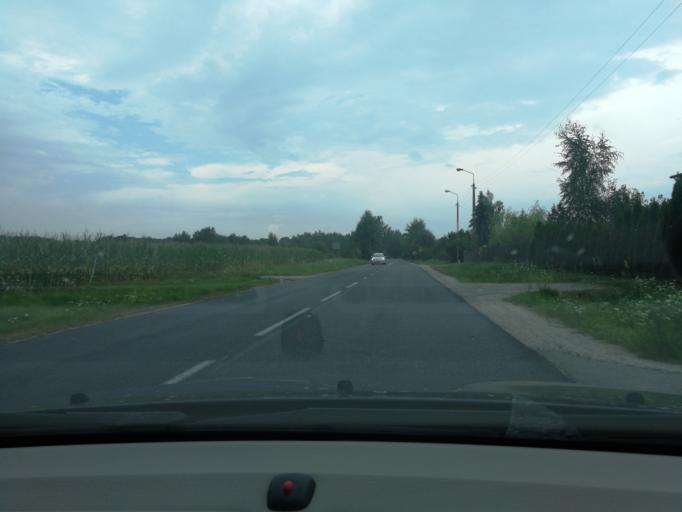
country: PL
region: Masovian Voivodeship
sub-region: Powiat zyrardowski
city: Radziejowice
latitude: 52.0099
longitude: 20.5591
